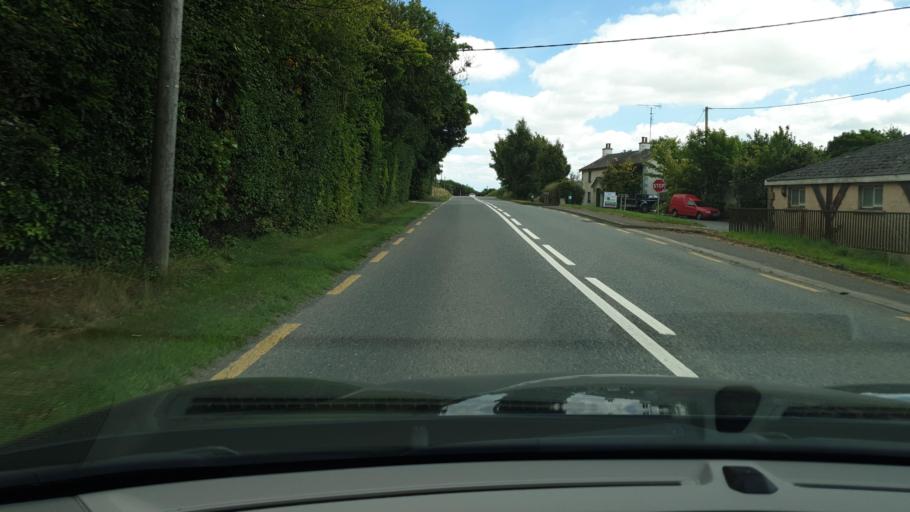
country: IE
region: Leinster
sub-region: An Mhi
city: Dunshaughlin
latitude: 53.5119
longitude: -6.6187
